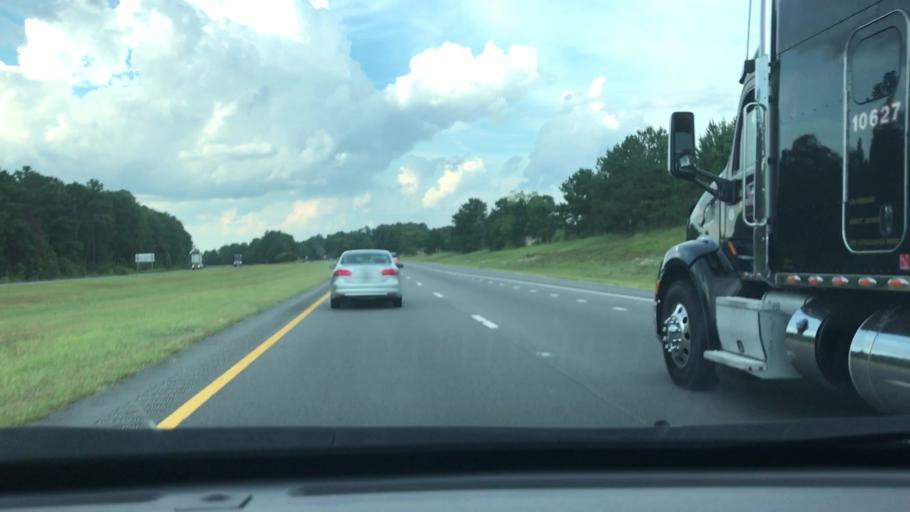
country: US
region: North Carolina
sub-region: Cumberland County
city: Vander
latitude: 35.0541
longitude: -78.7982
